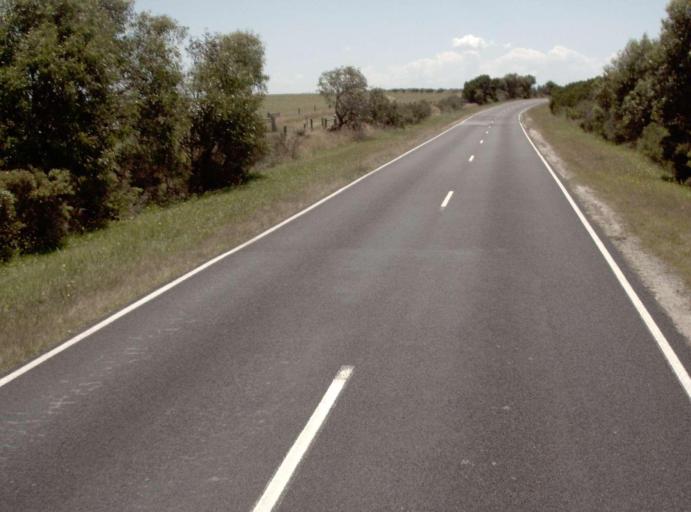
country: AU
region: Victoria
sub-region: Bass Coast
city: North Wonthaggi
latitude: -38.6206
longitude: 145.9598
